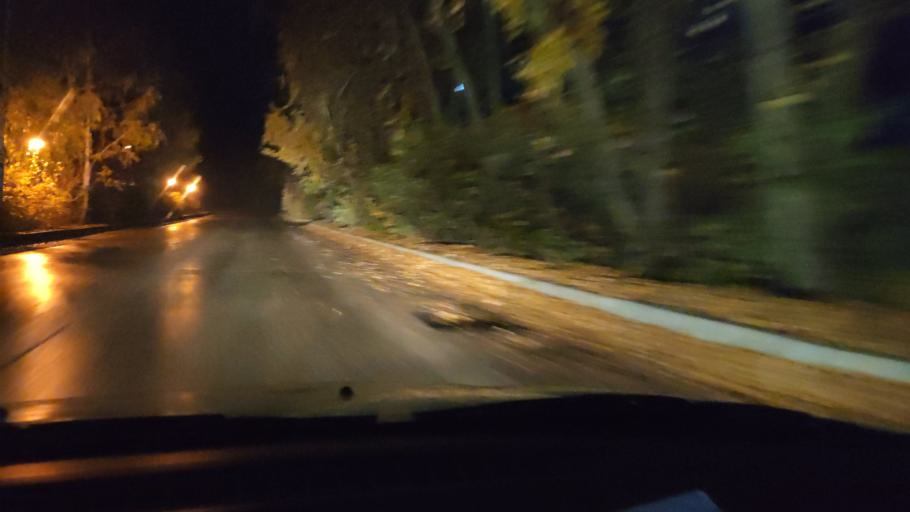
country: RU
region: Perm
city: Overyata
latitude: 58.0158
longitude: 55.9074
